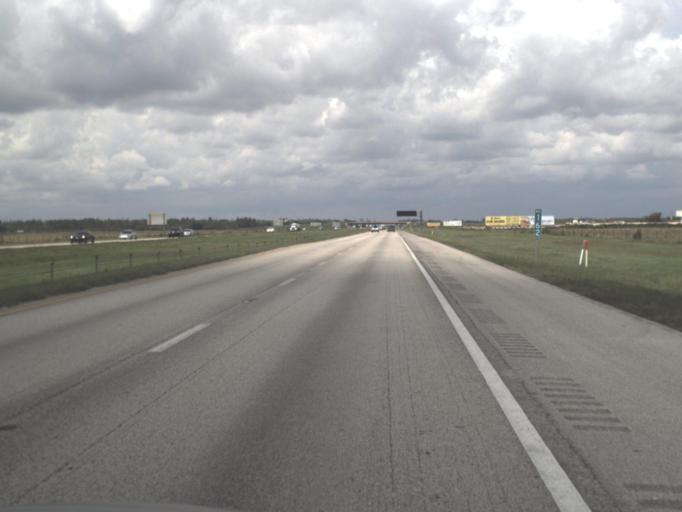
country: US
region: Florida
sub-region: Charlotte County
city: Punta Gorda
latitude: 26.9065
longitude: -82.0090
